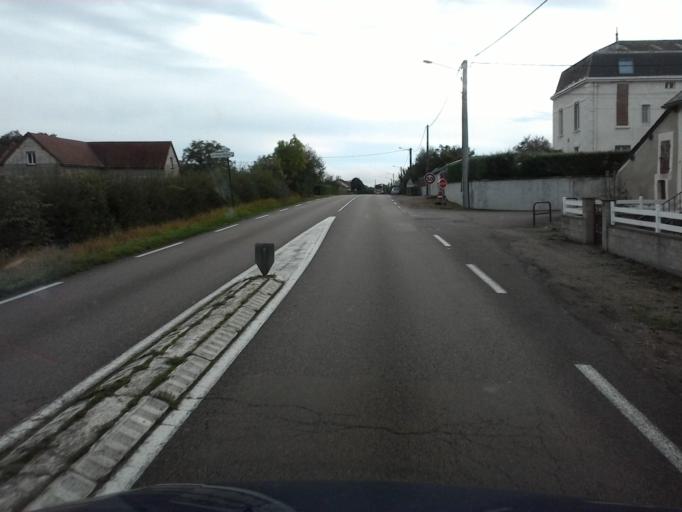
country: FR
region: Bourgogne
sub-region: Departement de Saone-et-Loire
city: Autun
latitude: 46.9966
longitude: 4.2338
